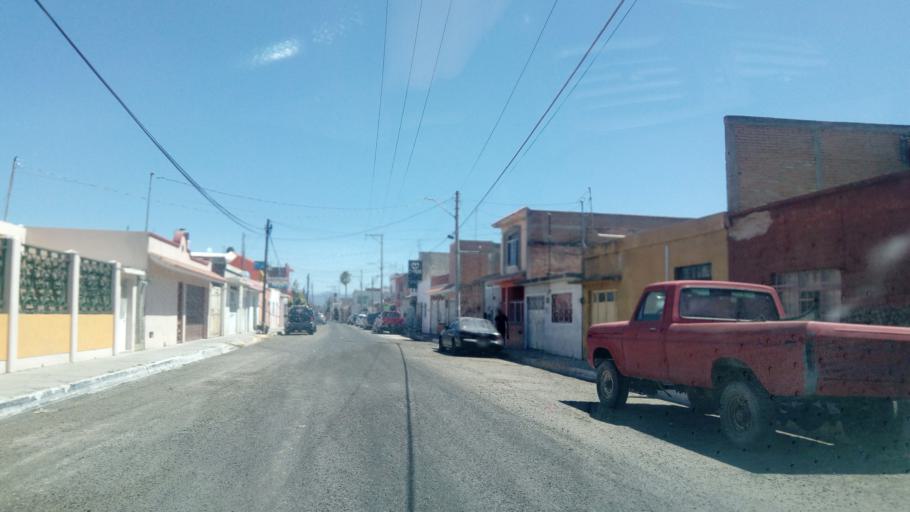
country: MX
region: Durango
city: Victoria de Durango
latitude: 24.0336
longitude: -104.6606
